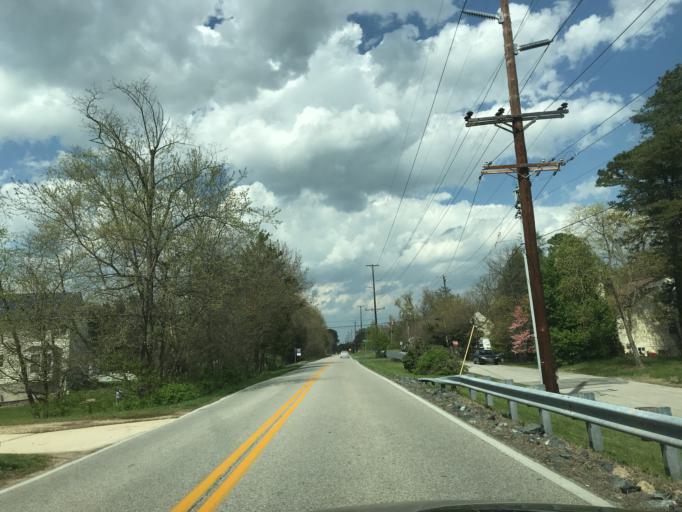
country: US
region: Maryland
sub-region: Anne Arundel County
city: Severn
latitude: 39.1232
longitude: -76.6783
